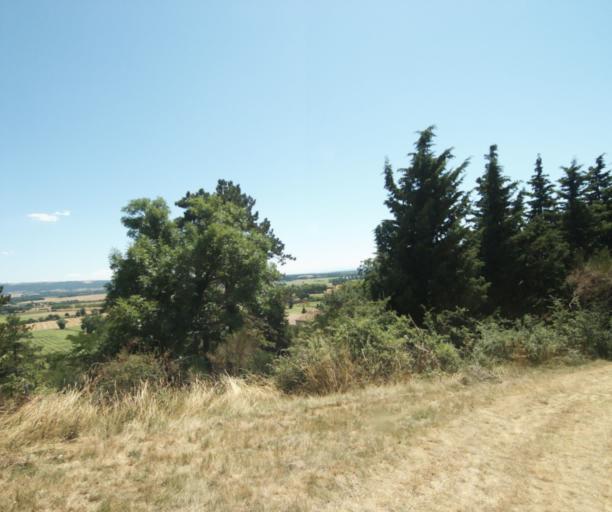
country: FR
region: Midi-Pyrenees
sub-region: Departement de la Haute-Garonne
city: Saint-Felix-Lauragais
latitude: 43.4552
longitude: 1.9086
